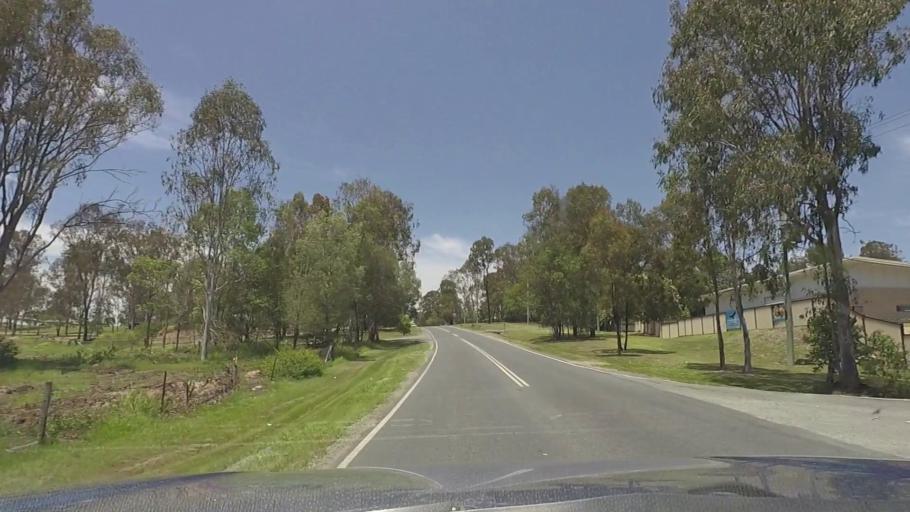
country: AU
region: Queensland
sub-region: Logan
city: North Maclean
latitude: -27.8258
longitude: 153.0257
